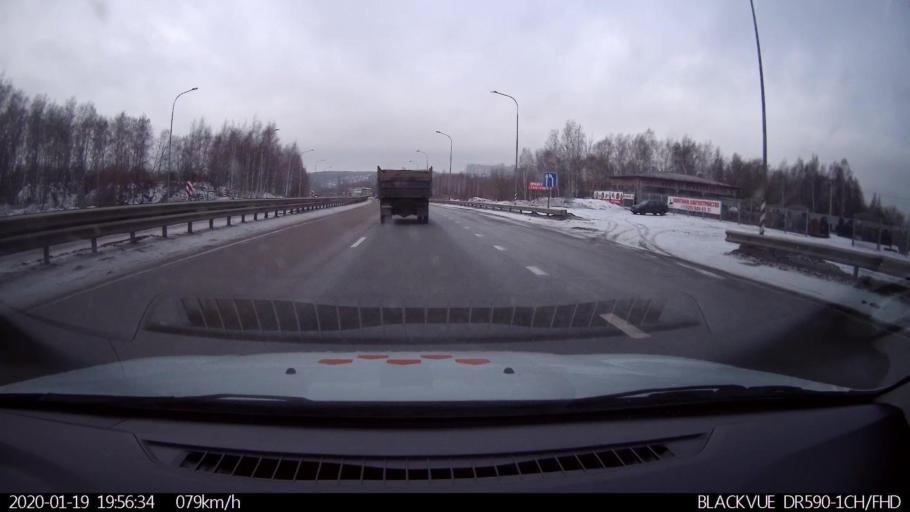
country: RU
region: Nizjnij Novgorod
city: Afonino
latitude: 56.2311
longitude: 44.0707
